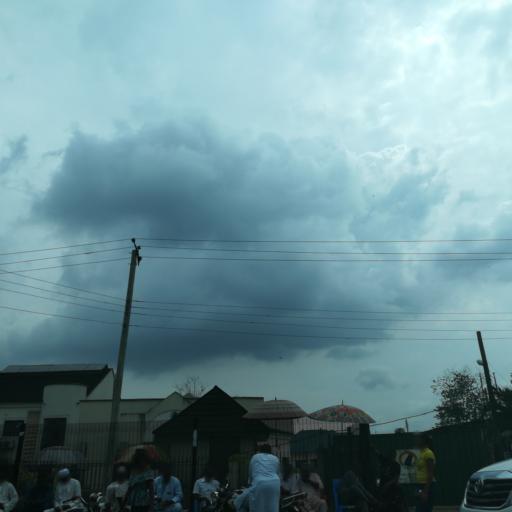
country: NG
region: Rivers
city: Port Harcourt
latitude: 4.8285
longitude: 7.0037
